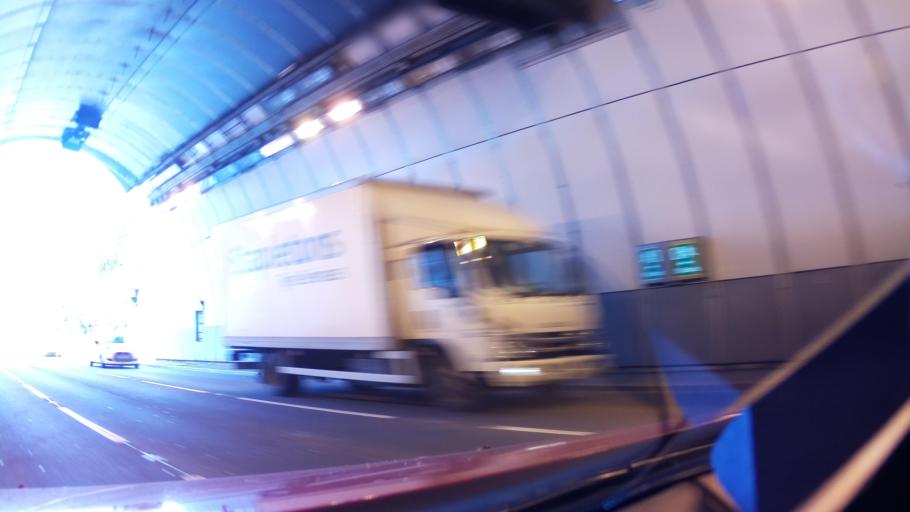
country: GB
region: England
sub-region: Cornwall
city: Saltash
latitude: 50.4123
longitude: -4.2166
